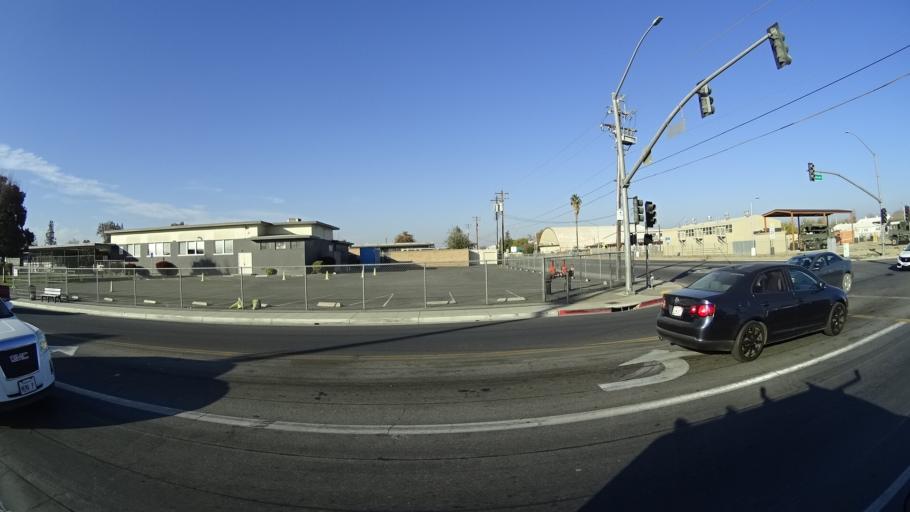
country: US
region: California
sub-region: Kern County
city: Bakersfield
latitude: 35.3394
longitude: -119.0123
